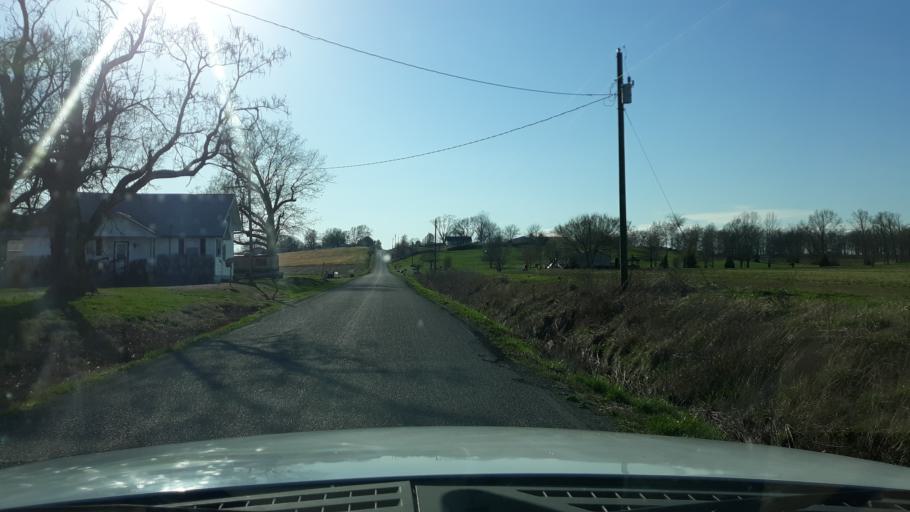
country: US
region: Illinois
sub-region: Saline County
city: Harrisburg
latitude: 37.7755
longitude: -88.5895
